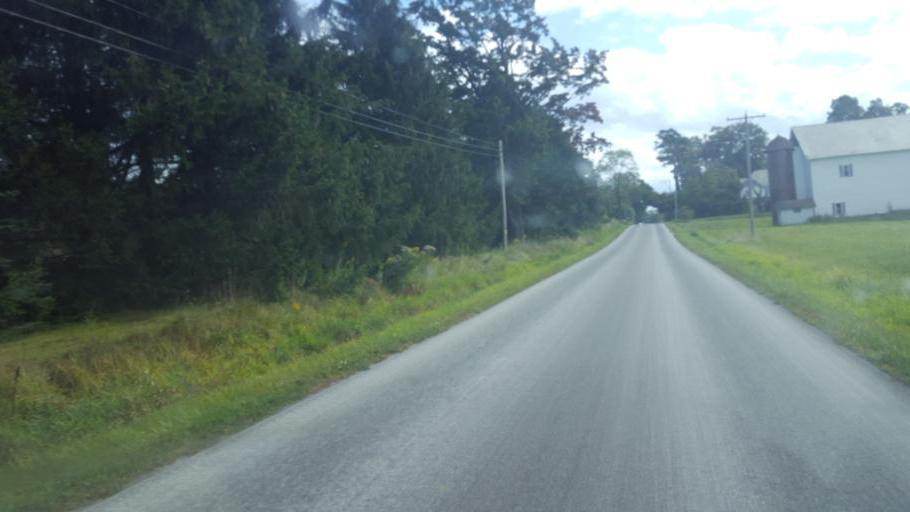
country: US
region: Pennsylvania
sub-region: Crawford County
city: Conneaut Lakeshore
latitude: 41.5040
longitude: -80.3136
